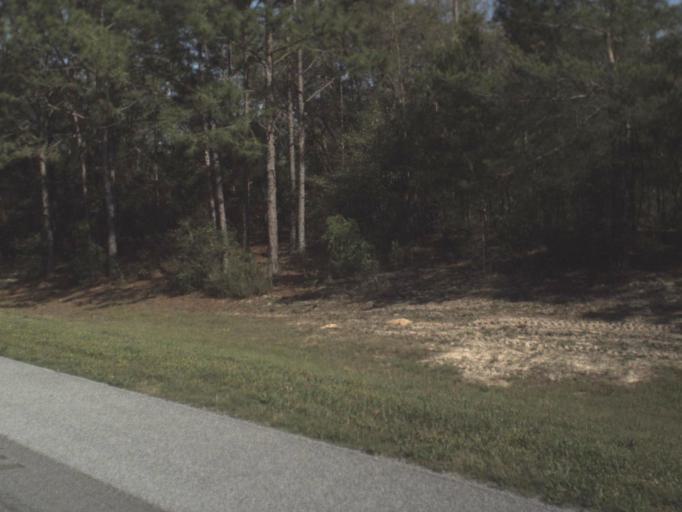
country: US
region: Florida
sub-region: Okaloosa County
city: Crestview
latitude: 30.7229
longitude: -86.4144
